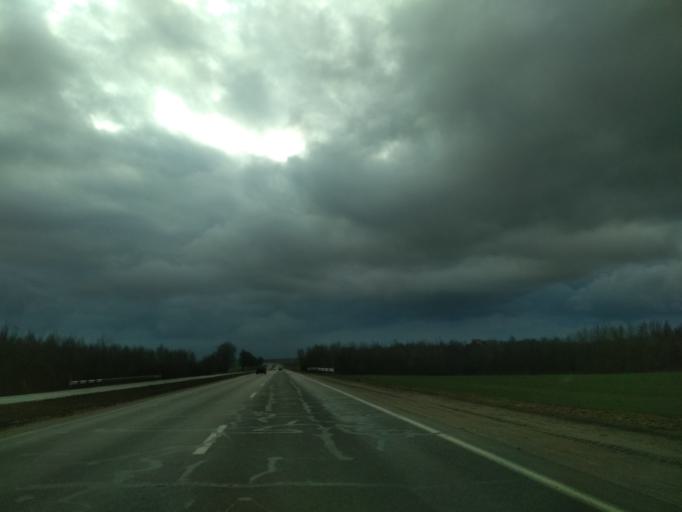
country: BY
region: Minsk
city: Luhavaya Slabada
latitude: 53.7628
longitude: 27.8284
